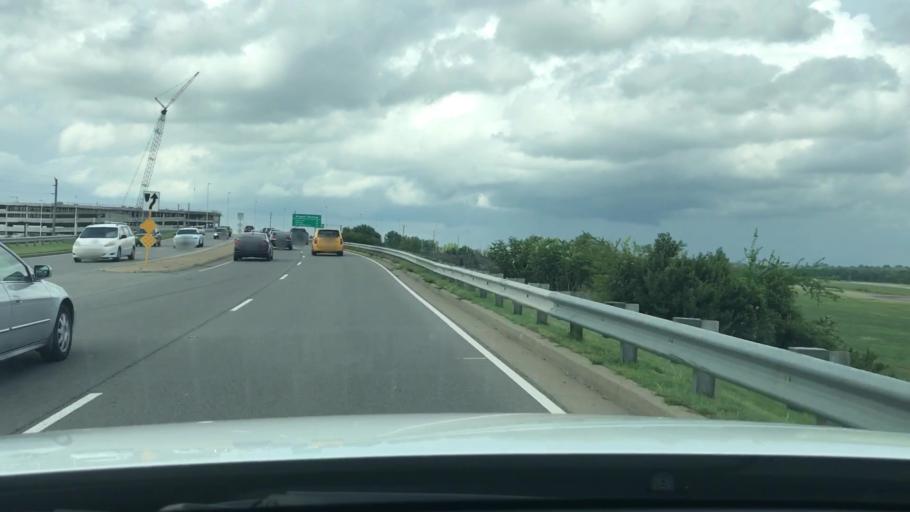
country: US
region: Tennessee
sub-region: Davidson County
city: Lakewood
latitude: 36.1261
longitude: -86.6651
